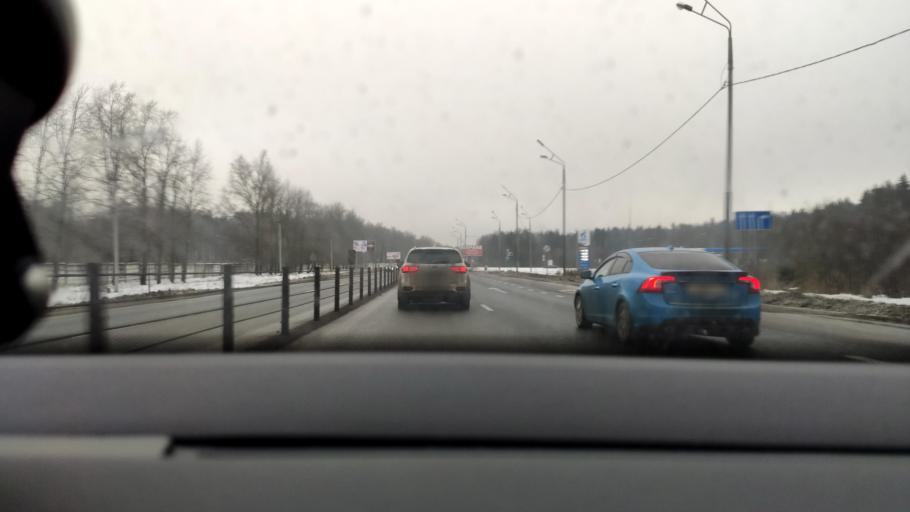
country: RU
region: Moskovskaya
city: Sergiyev Posad
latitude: 56.2509
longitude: 38.1229
